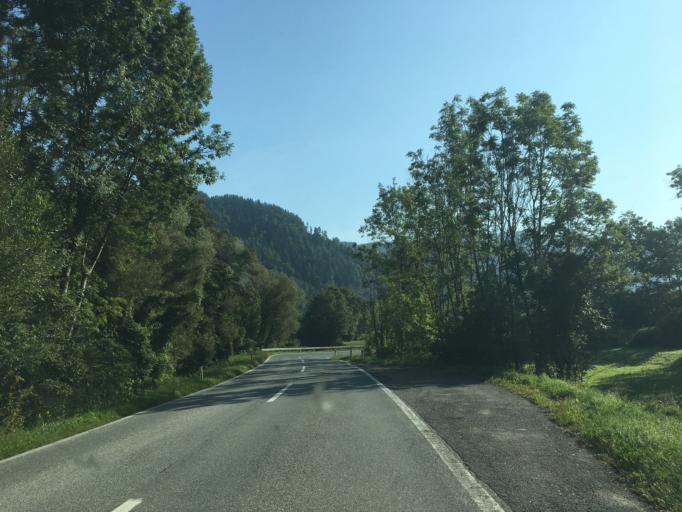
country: AT
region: Carinthia
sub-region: Politischer Bezirk Volkermarkt
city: Diex
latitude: 46.7013
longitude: 14.5819
